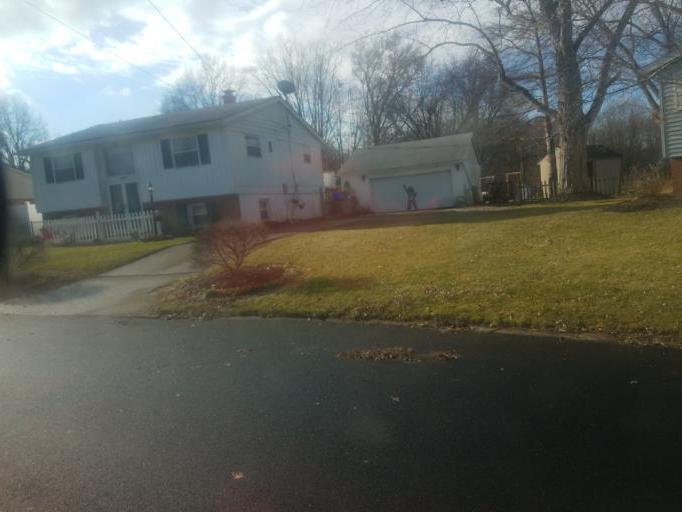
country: US
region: Ohio
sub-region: Marion County
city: Marion
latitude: 40.5668
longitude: -83.1591
